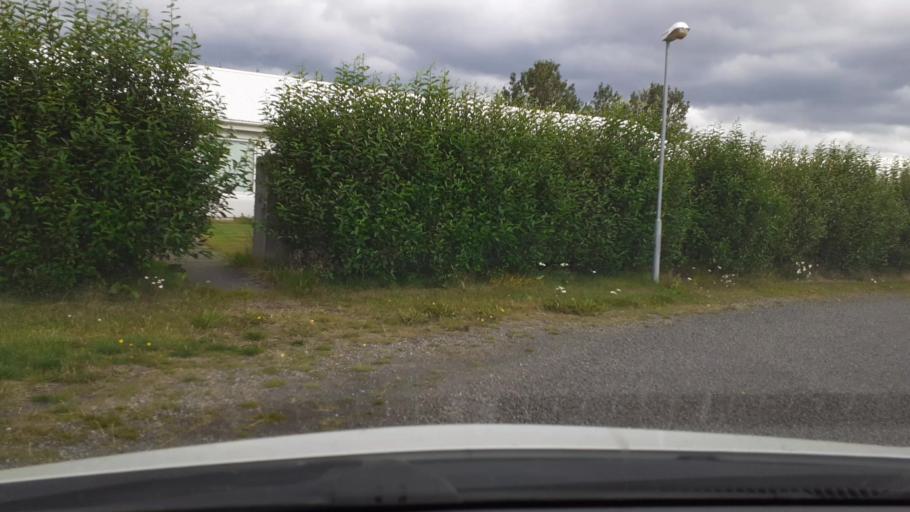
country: IS
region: West
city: Borgarnes
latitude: 64.5615
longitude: -21.7652
